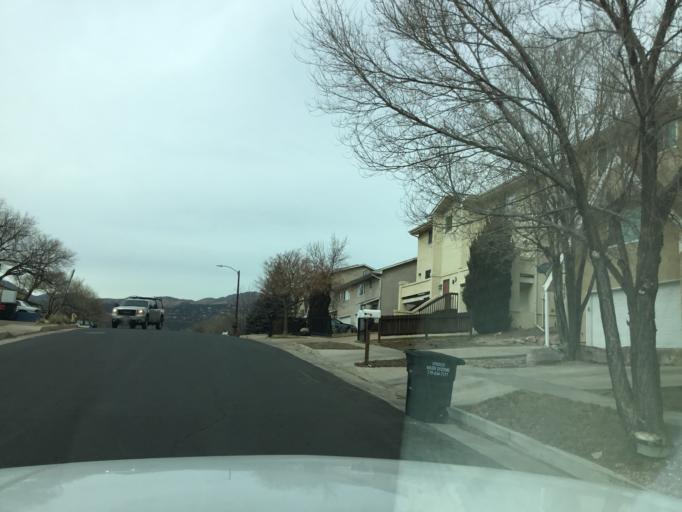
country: US
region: Colorado
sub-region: El Paso County
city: Colorado Springs
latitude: 38.8489
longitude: -104.8636
